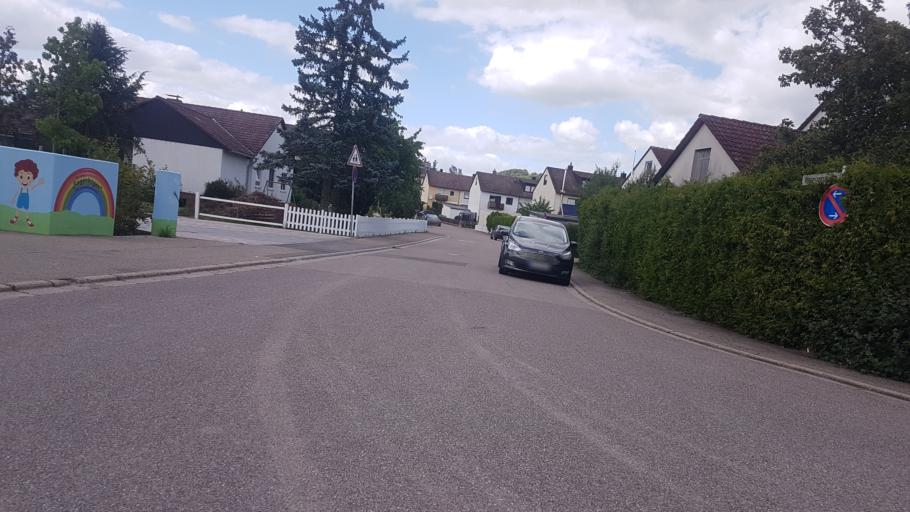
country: DE
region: Bavaria
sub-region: Regierungsbezirk Mittelfranken
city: Neusitz
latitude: 49.3710
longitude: 10.2268
